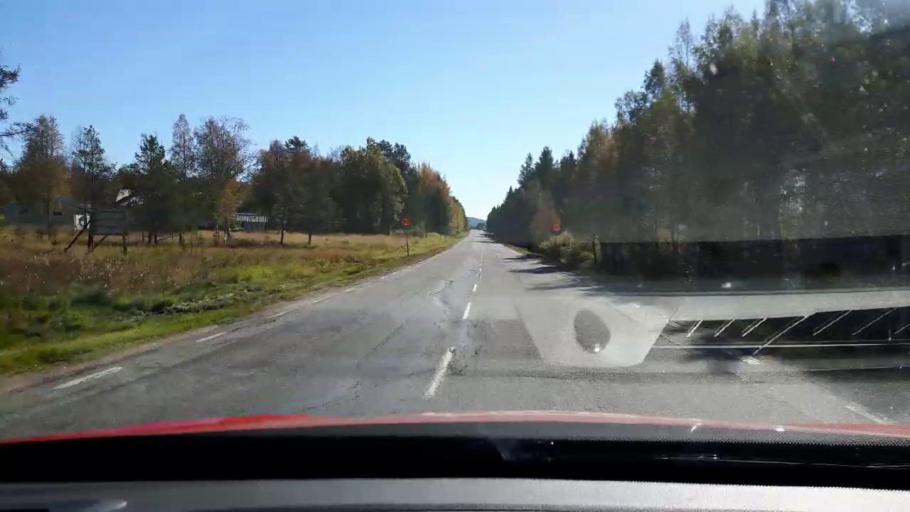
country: SE
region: Jaemtland
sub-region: Harjedalens Kommun
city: Sveg
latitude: 62.3093
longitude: 14.0423
